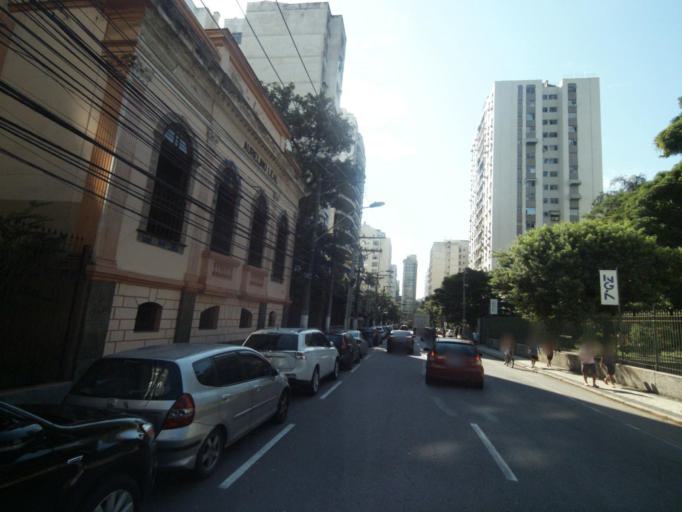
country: BR
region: Rio de Janeiro
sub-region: Niteroi
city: Niteroi
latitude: -22.9034
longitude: -43.1255
